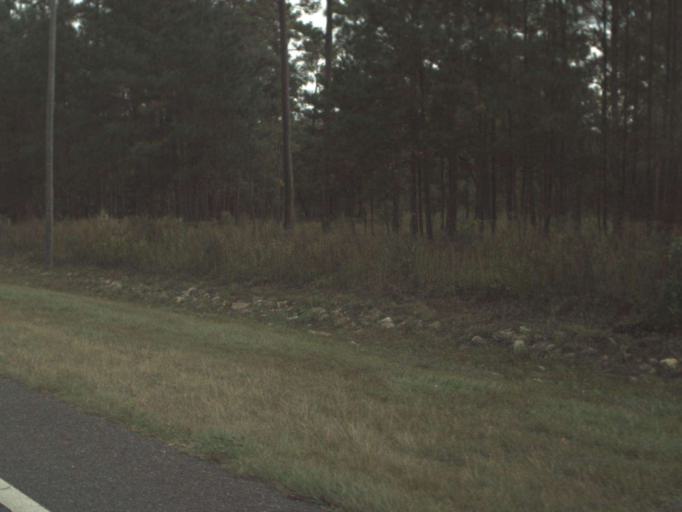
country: US
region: Florida
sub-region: Leon County
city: Tallahassee
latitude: 30.5856
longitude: -84.1956
